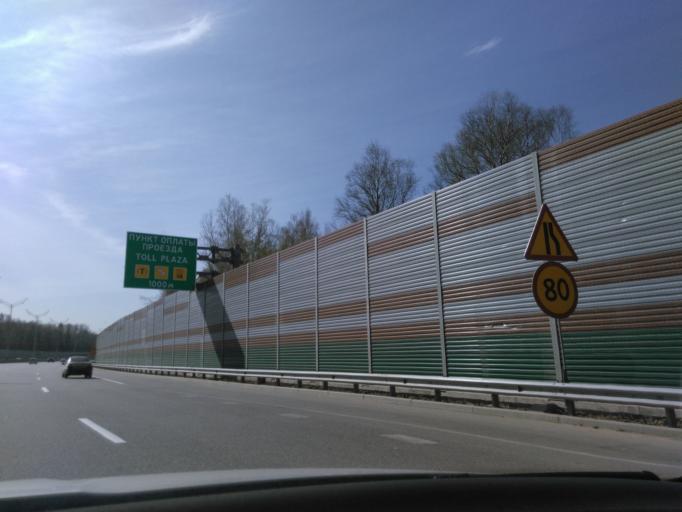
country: RU
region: Moscow
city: Khimki
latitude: 55.9444
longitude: 37.4451
